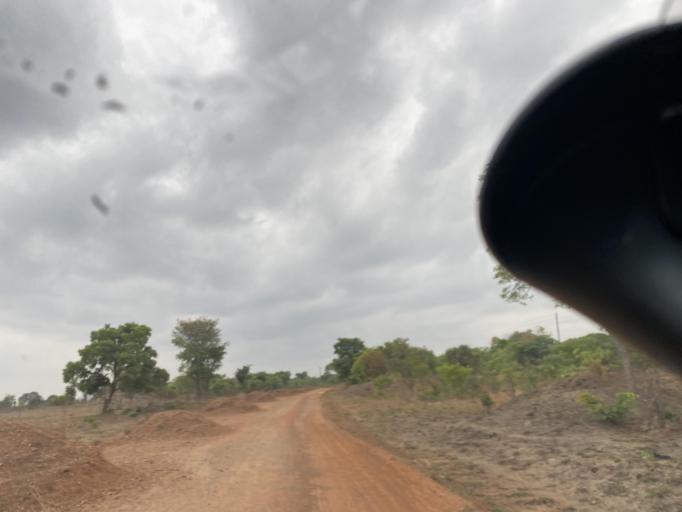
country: ZM
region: Lusaka
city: Chongwe
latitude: -15.2309
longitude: 28.7244
